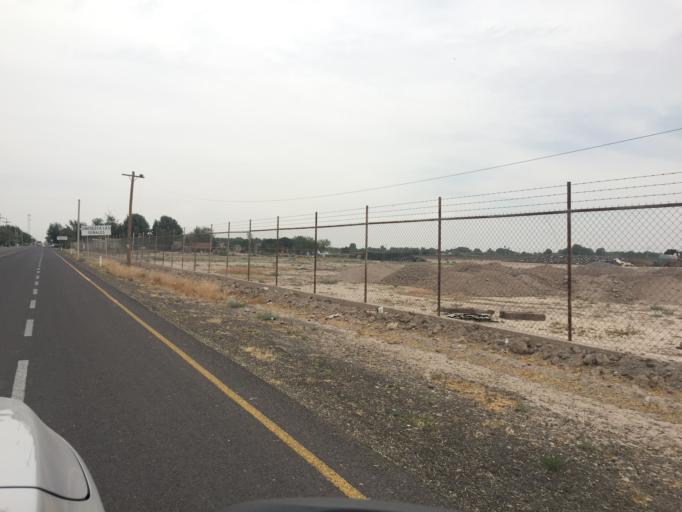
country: MX
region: Durango
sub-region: Gomez Palacio
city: San Jose de Vinedo
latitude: 25.6781
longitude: -103.4447
